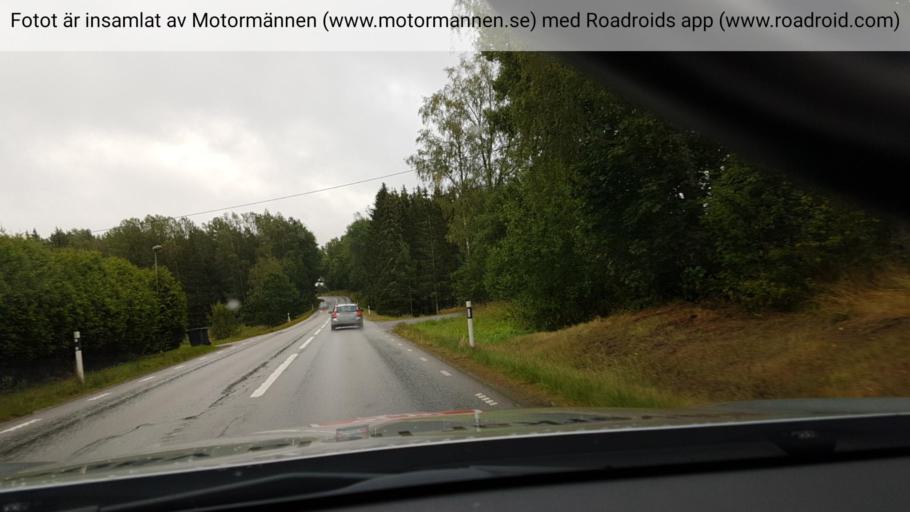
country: SE
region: Vaestra Goetaland
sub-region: Alingsas Kommun
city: Sollebrunn
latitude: 58.1153
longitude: 12.5585
